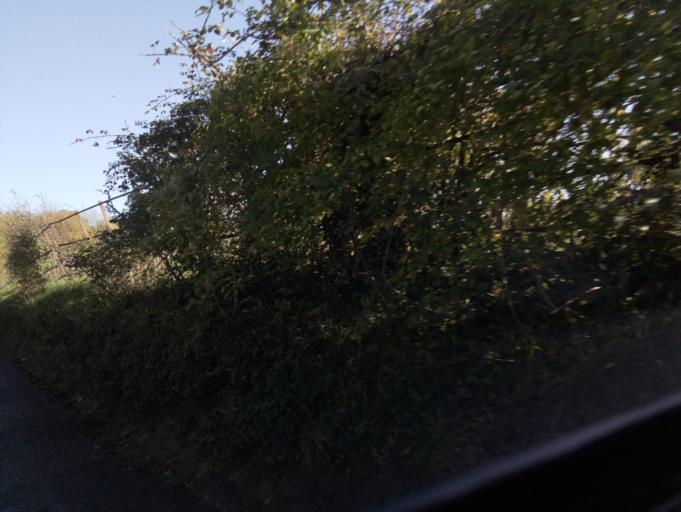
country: GB
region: England
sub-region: Somerset
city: Bruton
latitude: 51.1217
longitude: -2.4456
